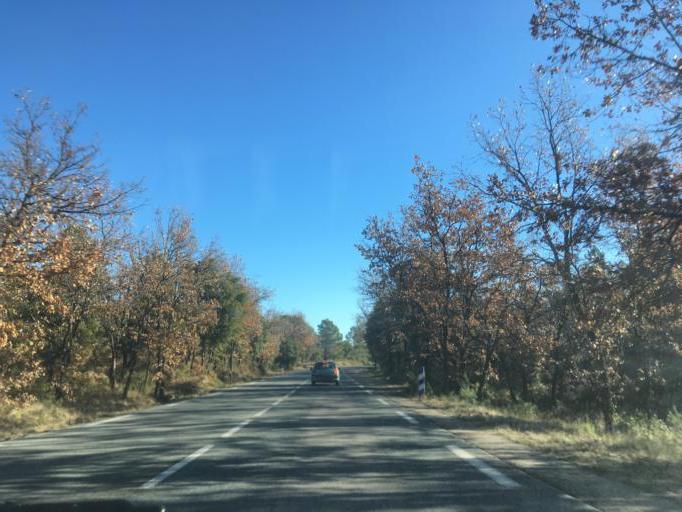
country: FR
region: Provence-Alpes-Cote d'Azur
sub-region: Departement du Var
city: Lorgues
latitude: 43.5457
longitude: 6.3347
